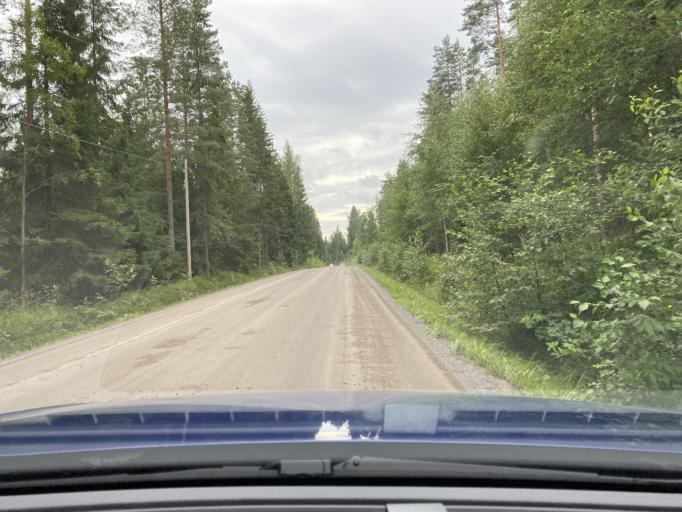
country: FI
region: Satakunta
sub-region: Rauma
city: Kiukainen
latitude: 61.1372
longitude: 21.9911
